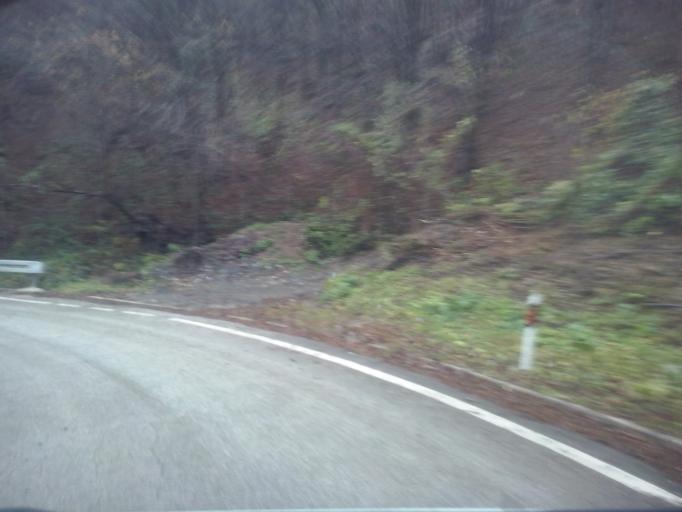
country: RS
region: Central Serbia
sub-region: Moravicki Okrug
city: Ivanjica
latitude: 43.5389
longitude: 20.2810
